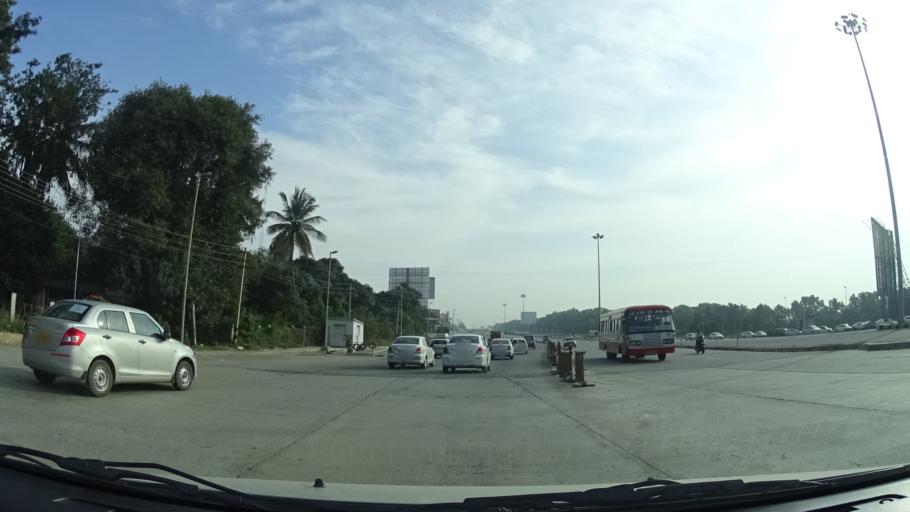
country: IN
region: Karnataka
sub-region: Bangalore Rural
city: Devanhalli
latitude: 13.1941
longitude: 77.6502
